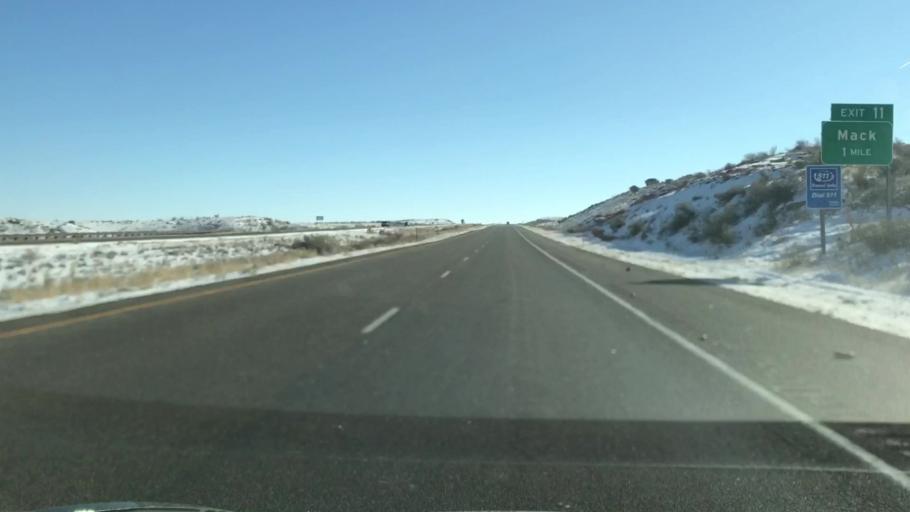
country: US
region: Colorado
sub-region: Mesa County
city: Loma
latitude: 39.2221
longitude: -108.8886
